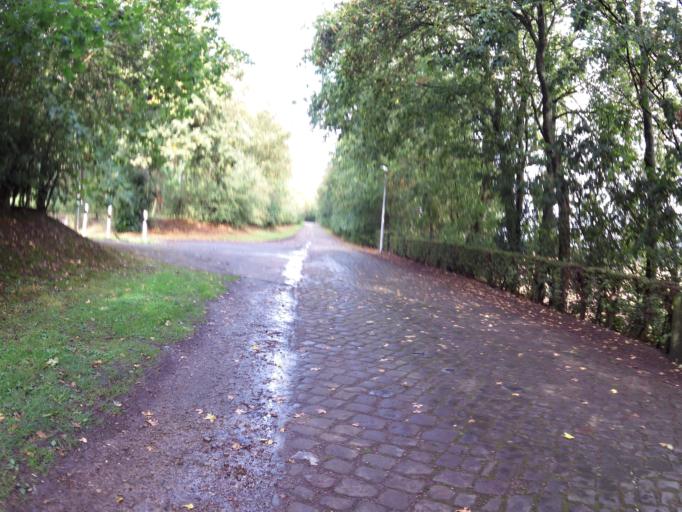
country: DE
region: Lower Saxony
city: Balge
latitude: 52.7219
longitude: 9.1946
